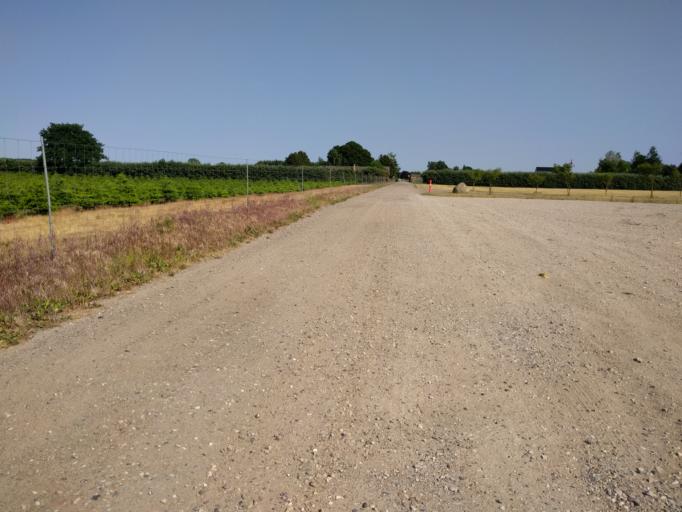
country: DK
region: South Denmark
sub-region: Kerteminde Kommune
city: Langeskov
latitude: 55.3976
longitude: 10.5501
